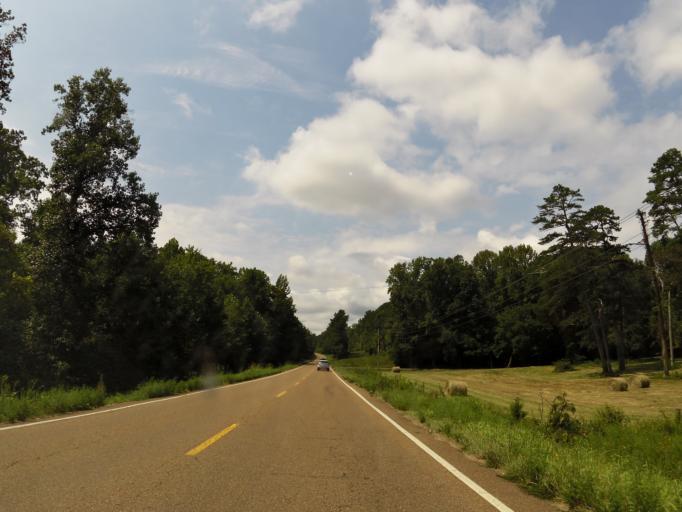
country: US
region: Tennessee
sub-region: Decatur County
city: Decaturville
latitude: 35.5433
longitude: -88.2030
